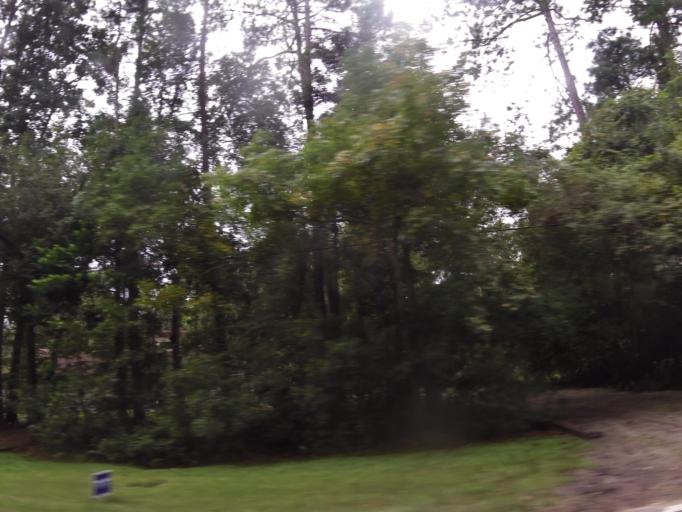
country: US
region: Florida
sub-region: Clay County
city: Bellair-Meadowbrook Terrace
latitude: 30.2569
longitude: -81.7234
